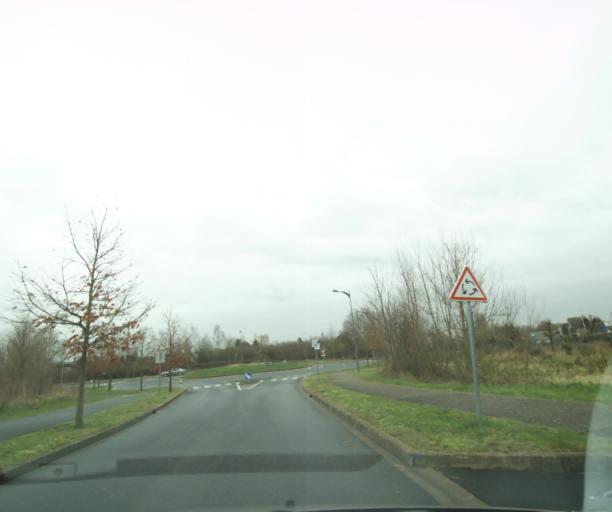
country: FR
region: Picardie
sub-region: Departement de l'Oise
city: Noyon
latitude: 49.5787
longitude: 3.0233
